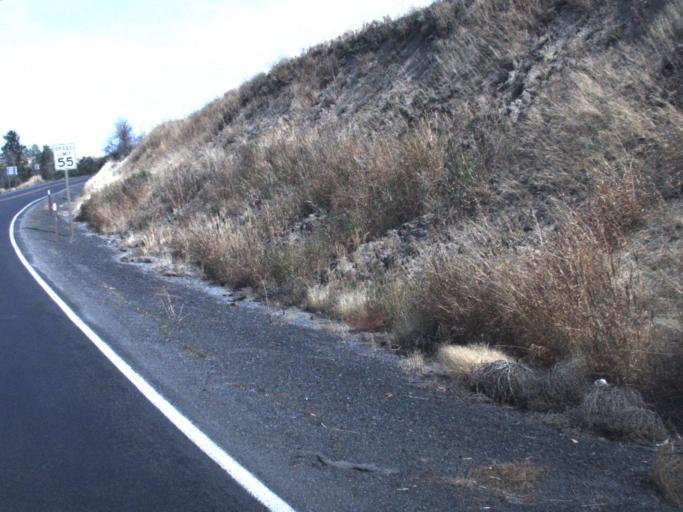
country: US
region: Idaho
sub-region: Benewah County
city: Plummer
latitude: 47.3355
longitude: -117.1921
